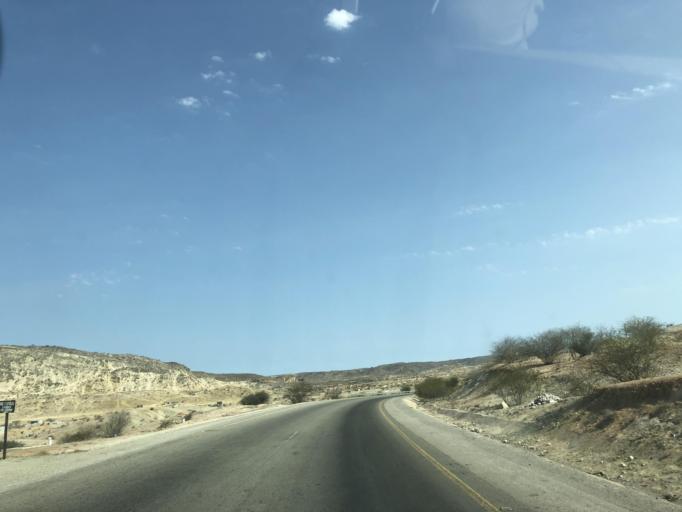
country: AO
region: Benguela
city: Benguela
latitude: -12.7228
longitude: 13.3482
